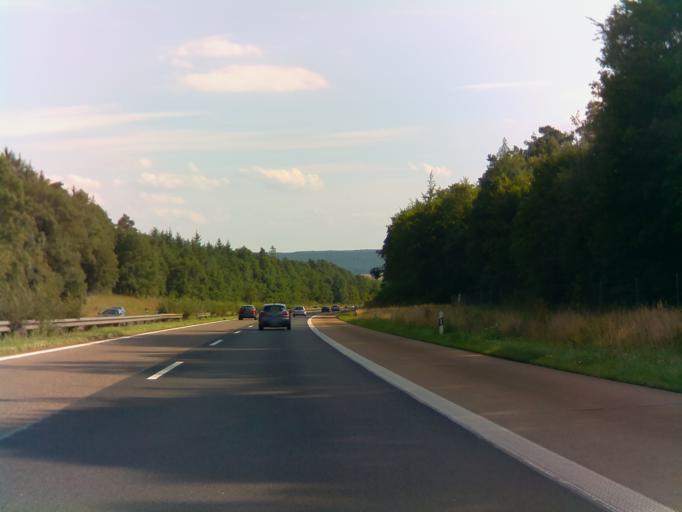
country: DE
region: Bavaria
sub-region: Regierungsbezirk Unterfranken
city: Elfershausen
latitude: 50.1709
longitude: 9.9628
